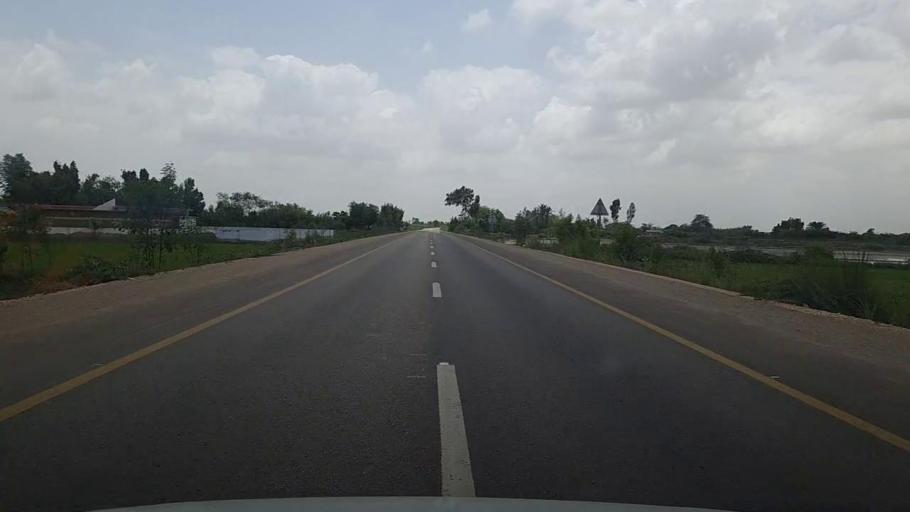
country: PK
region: Sindh
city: Thatta
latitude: 24.7464
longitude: 67.9511
